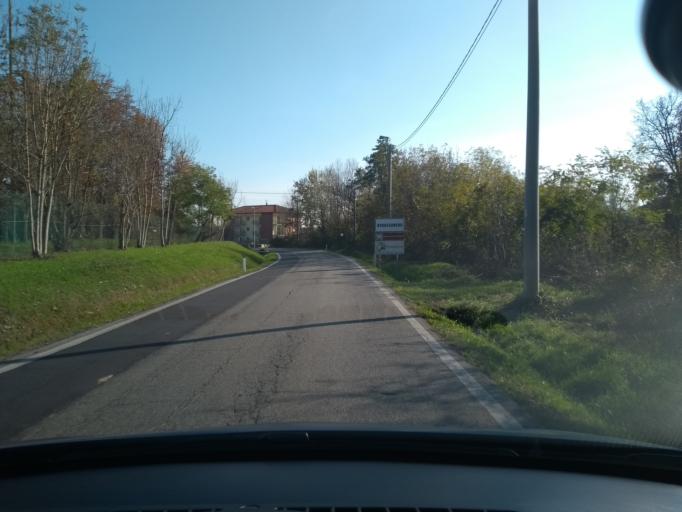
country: IT
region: Piedmont
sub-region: Provincia di Torino
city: Robassomero
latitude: 45.2043
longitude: 7.5584
